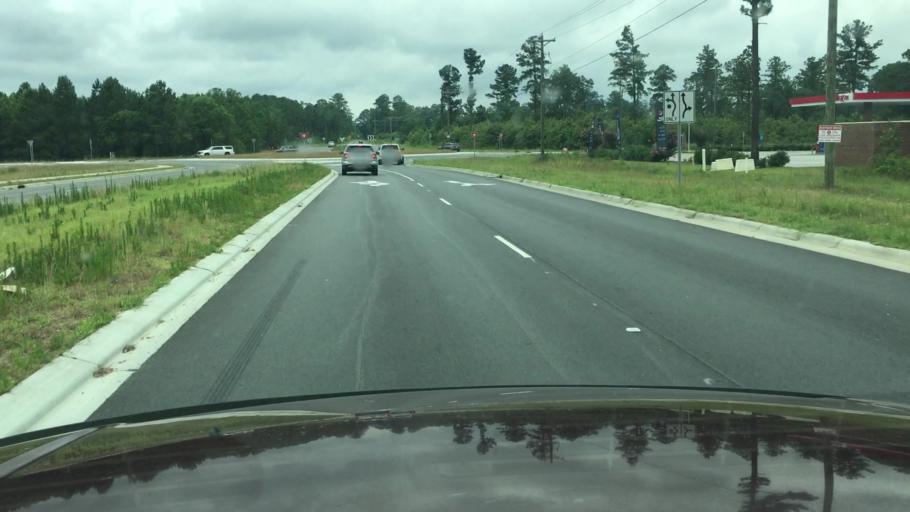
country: US
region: North Carolina
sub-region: Cumberland County
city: Spring Lake
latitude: 35.2579
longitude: -78.9694
